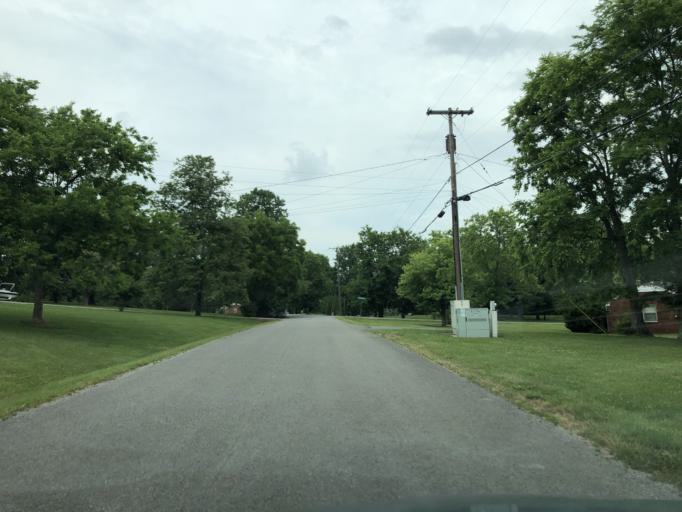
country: US
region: Tennessee
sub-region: Davidson County
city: Goodlettsville
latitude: 36.2660
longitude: -86.7646
